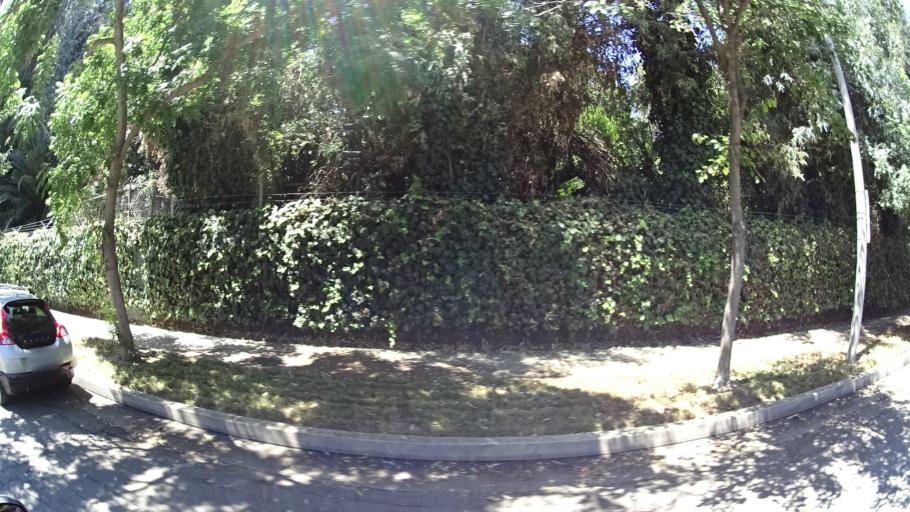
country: US
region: California
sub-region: Los Angeles County
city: Universal City
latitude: 34.1495
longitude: -118.3334
